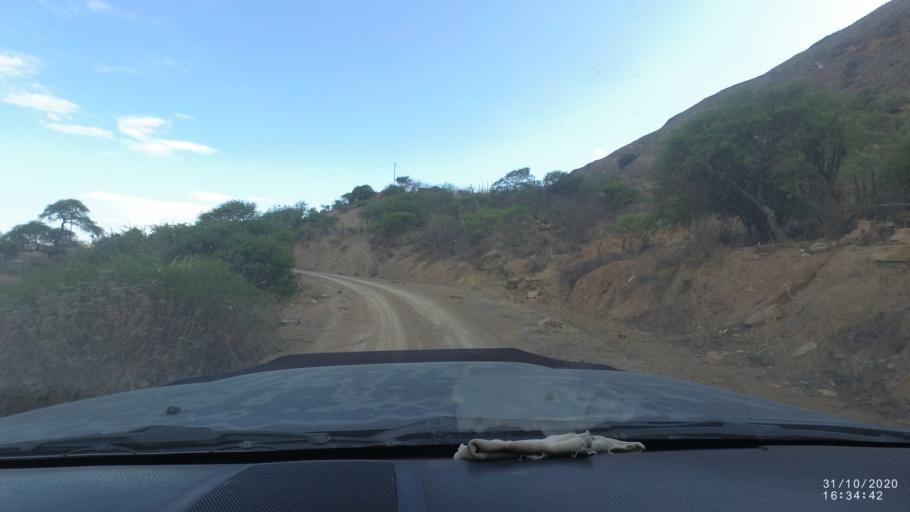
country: BO
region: Chuquisaca
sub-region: Provincia Zudanez
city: Mojocoya
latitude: -18.4496
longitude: -64.5839
